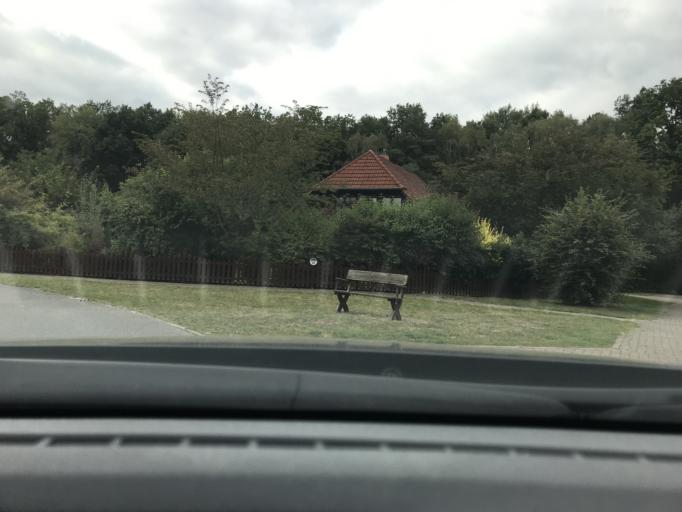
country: DE
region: Lower Saxony
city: Suderburg
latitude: 52.8968
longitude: 10.4662
